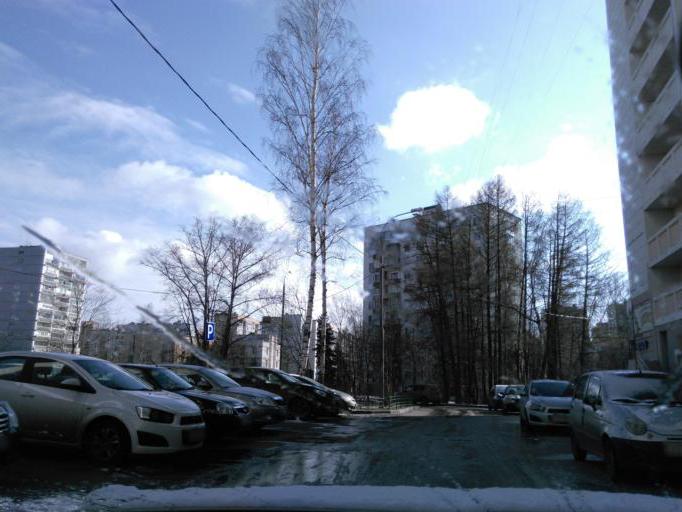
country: RU
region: Moscow
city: Zelenograd
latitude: 55.9998
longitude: 37.2022
